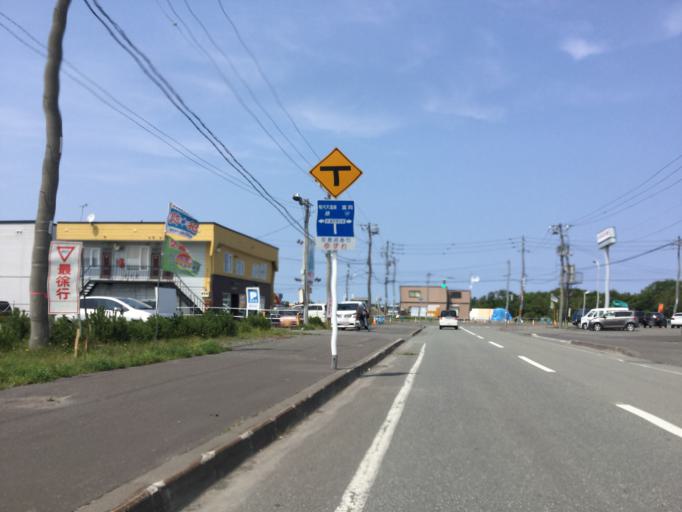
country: JP
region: Hokkaido
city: Wakkanai
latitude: 45.3858
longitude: 141.7042
